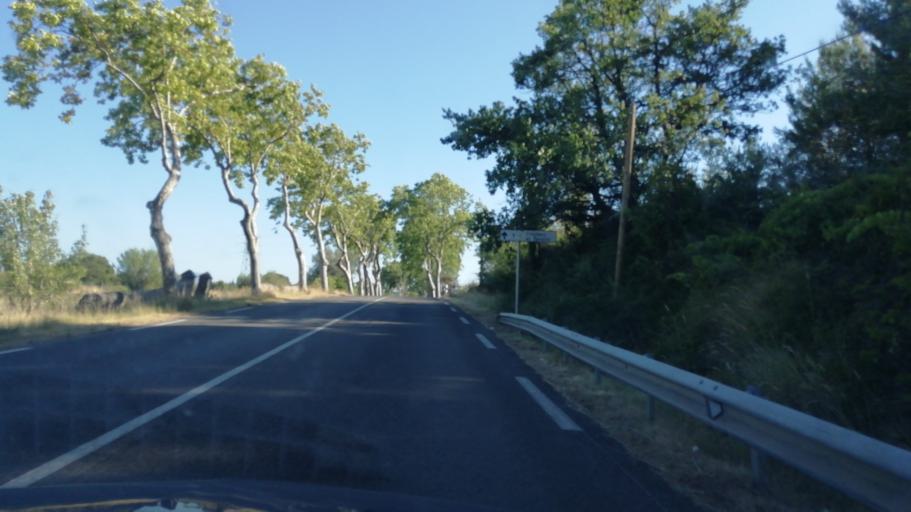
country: FR
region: Languedoc-Roussillon
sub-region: Departement de l'Herault
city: Nebian
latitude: 43.6144
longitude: 3.4368
